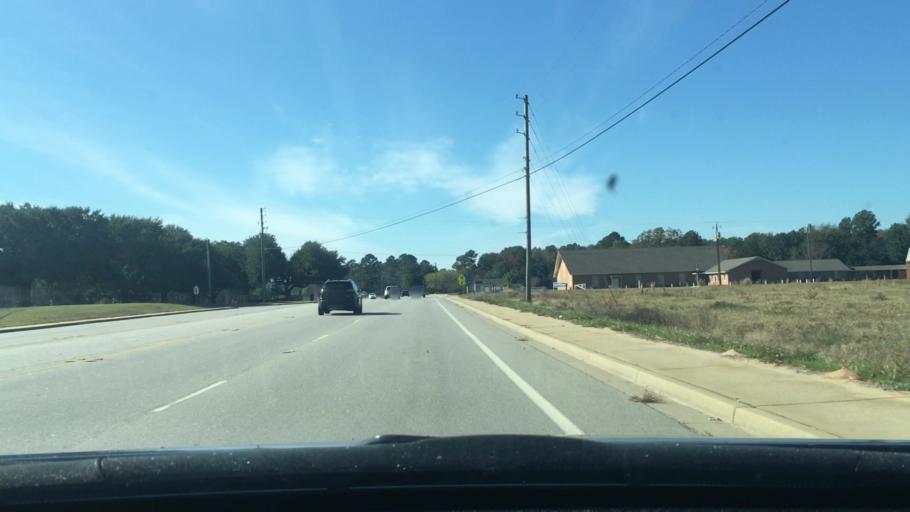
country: US
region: South Carolina
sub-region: Sumter County
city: South Sumter
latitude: 33.9012
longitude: -80.3933
